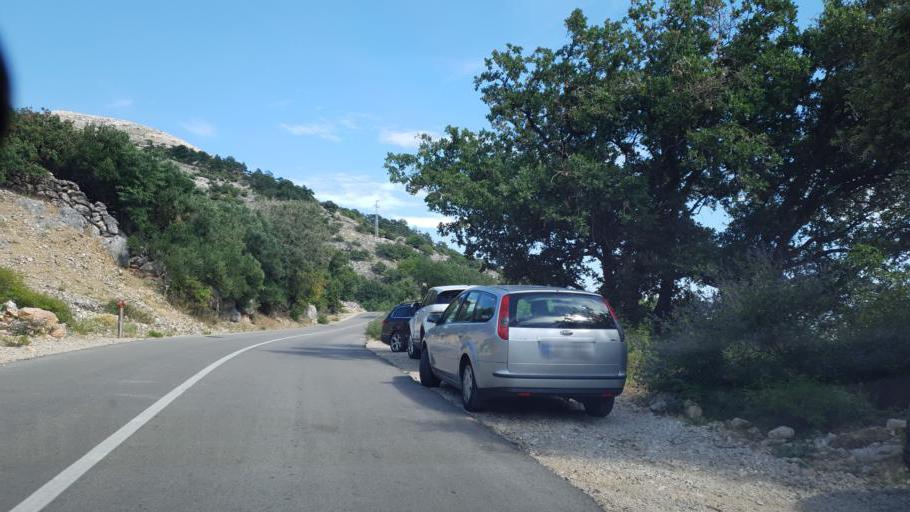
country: HR
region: Primorsko-Goranska
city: Punat
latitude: 44.9663
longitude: 14.6779
